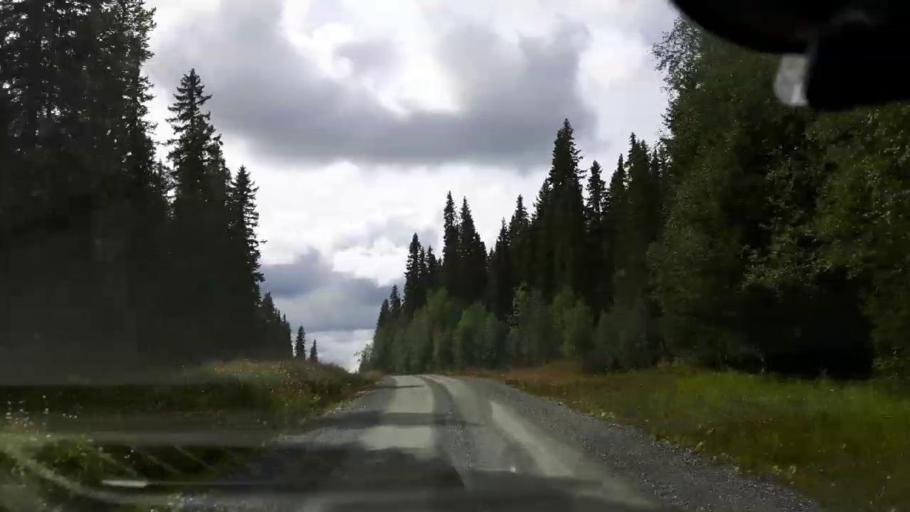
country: SE
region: Jaemtland
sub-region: Krokoms Kommun
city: Valla
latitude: 63.5730
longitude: 13.8813
